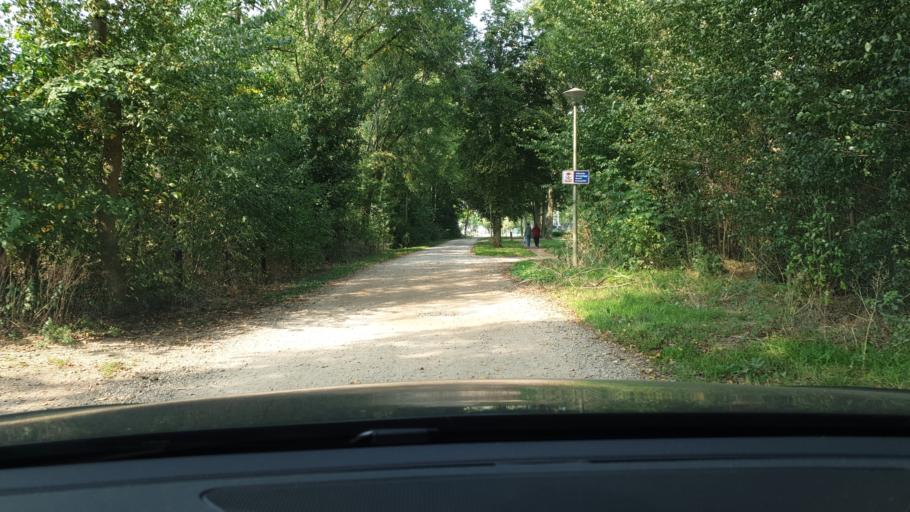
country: NL
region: Gelderland
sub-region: Gemeente Zevenaar
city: Zevenaar
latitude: 51.8568
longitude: 6.0510
